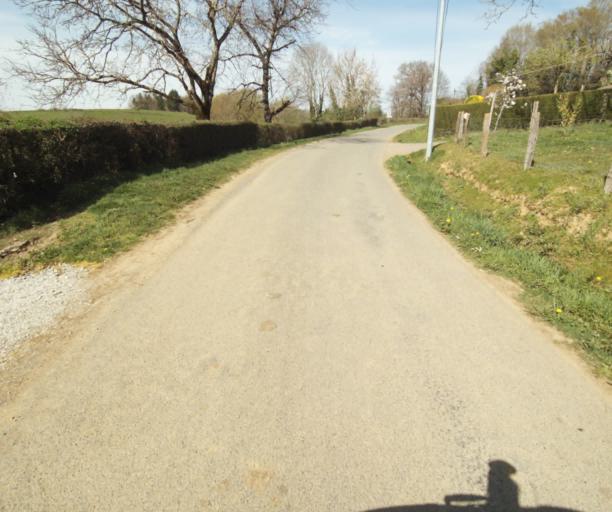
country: FR
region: Limousin
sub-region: Departement de la Correze
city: Naves
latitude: 45.3571
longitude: 1.7787
